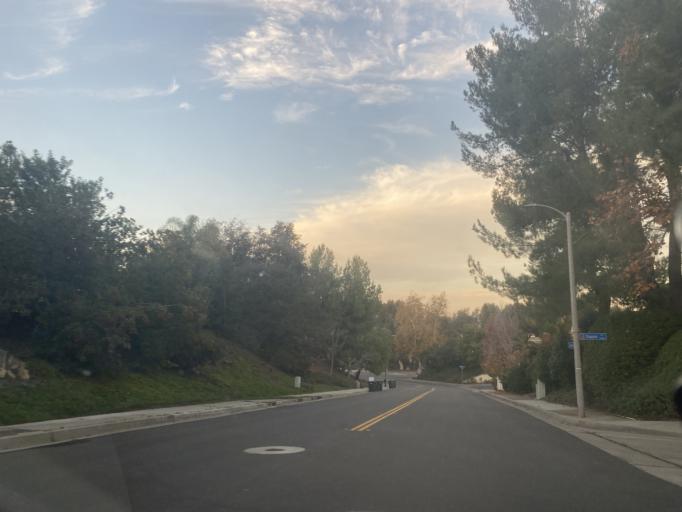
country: US
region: California
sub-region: Orange County
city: North Tustin
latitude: 33.7949
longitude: -117.7774
